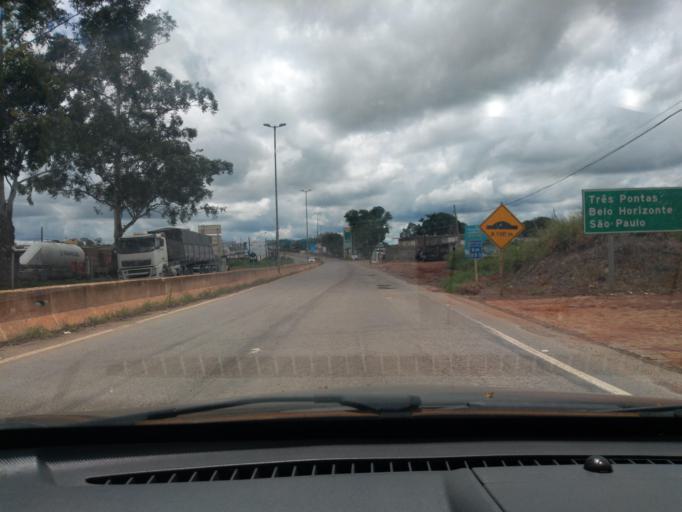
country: BR
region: Minas Gerais
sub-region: Lavras
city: Lavras
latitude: -21.2373
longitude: -45.0262
